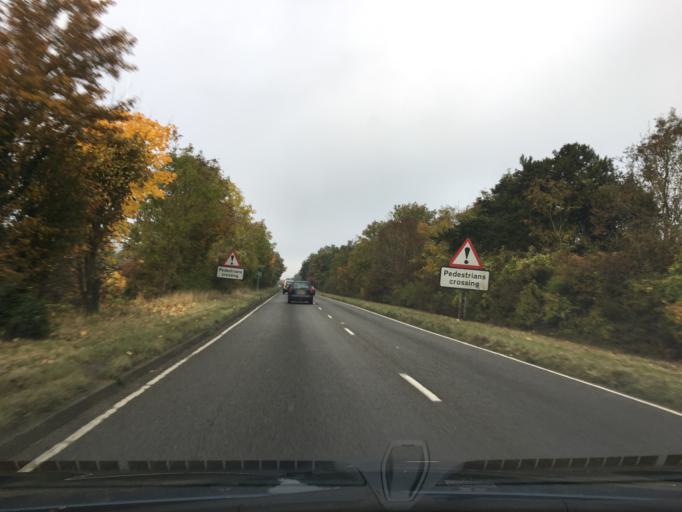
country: GB
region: England
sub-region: Surrey
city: Seale
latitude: 51.2267
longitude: -0.7125
